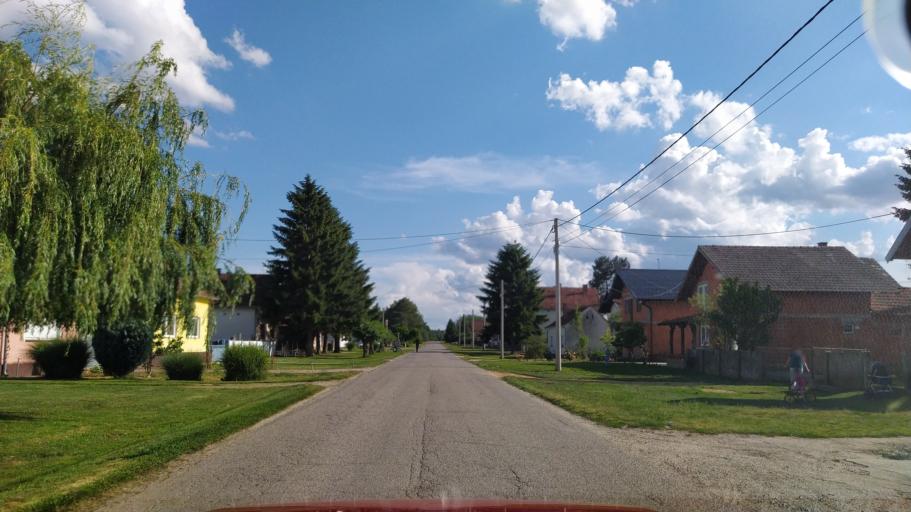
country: HR
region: Virovitick-Podravska
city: Pitomaca
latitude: 45.9597
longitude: 17.2147
